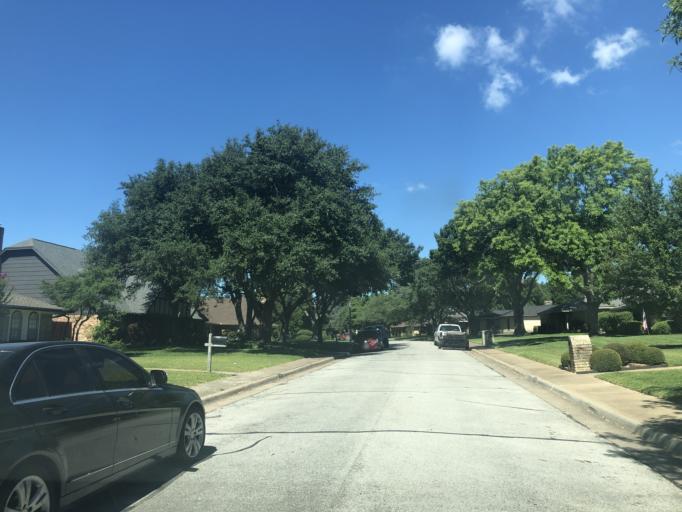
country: US
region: Texas
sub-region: Dallas County
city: Duncanville
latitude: 32.6386
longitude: -96.9273
